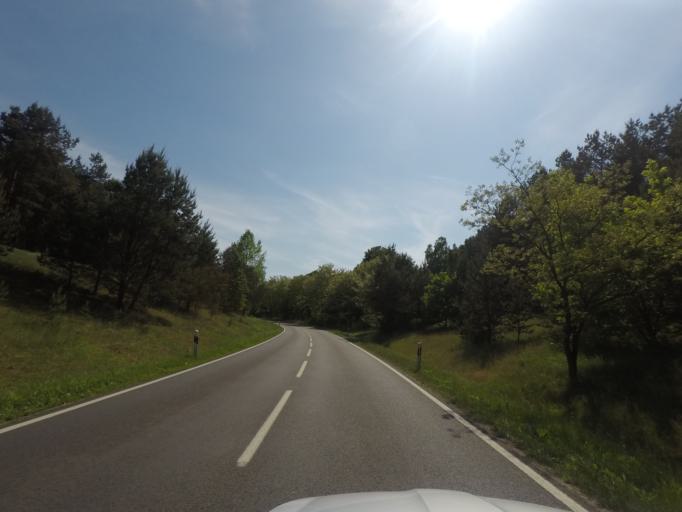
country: DE
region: Brandenburg
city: Britz
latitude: 52.8615
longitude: 13.7959
